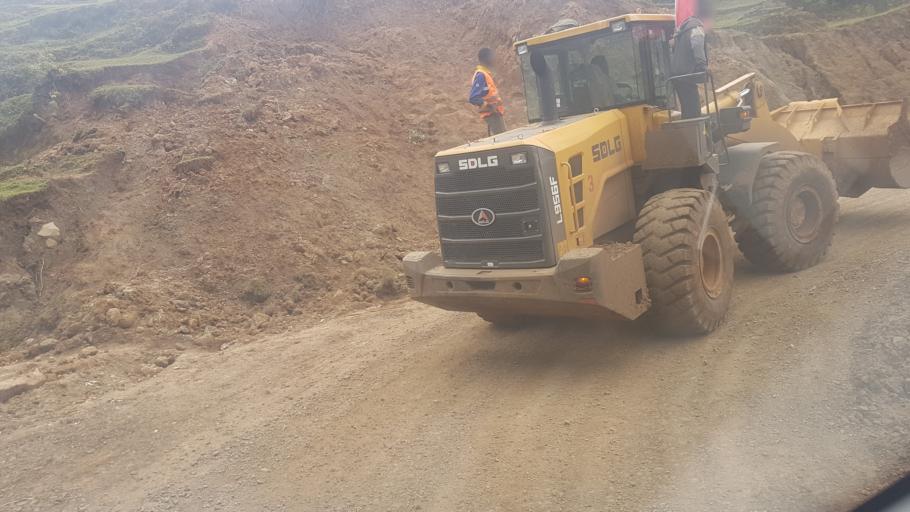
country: ET
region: Southern Nations, Nationalities, and People's Region
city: Arba Minch'
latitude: 6.3226
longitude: 37.5393
